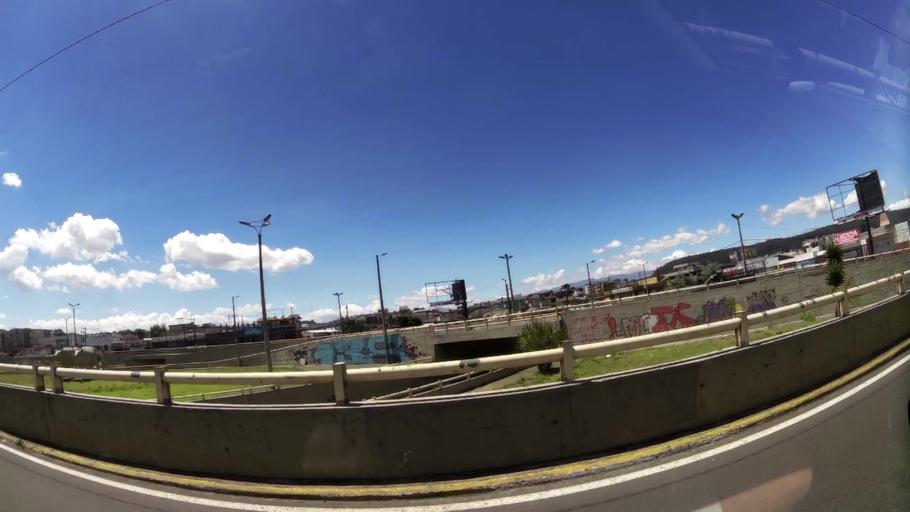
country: EC
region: Pichincha
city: Quito
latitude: -0.1573
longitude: -78.4854
